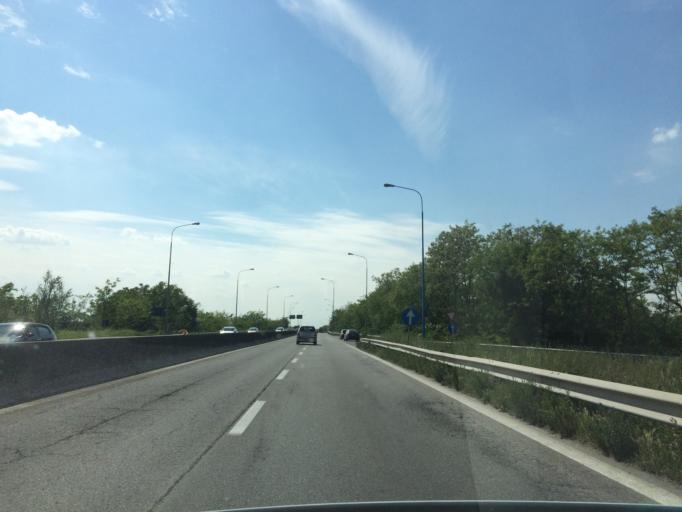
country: IT
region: Lombardy
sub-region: Provincia di Brescia
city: Buffalora-Bettole
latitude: 45.5013
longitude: 10.2775
